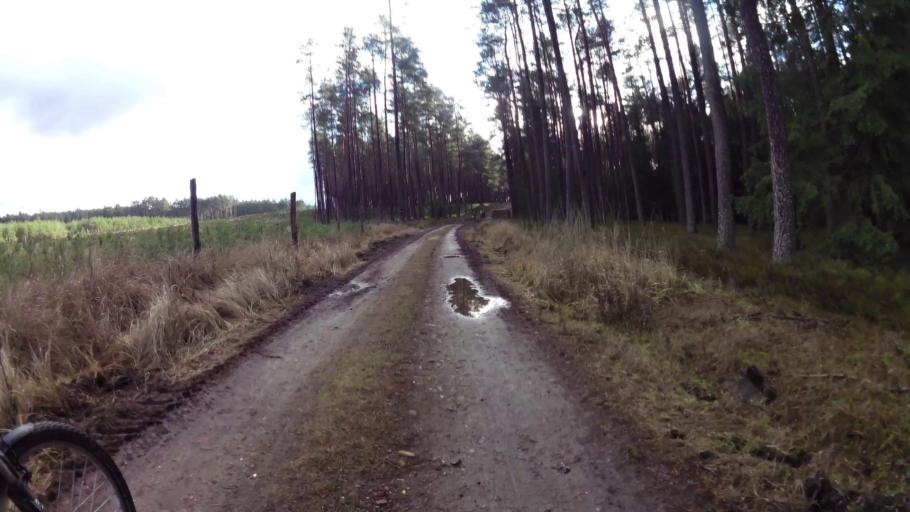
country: PL
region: West Pomeranian Voivodeship
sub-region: Powiat koszalinski
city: Sianow
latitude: 54.0923
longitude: 16.2939
